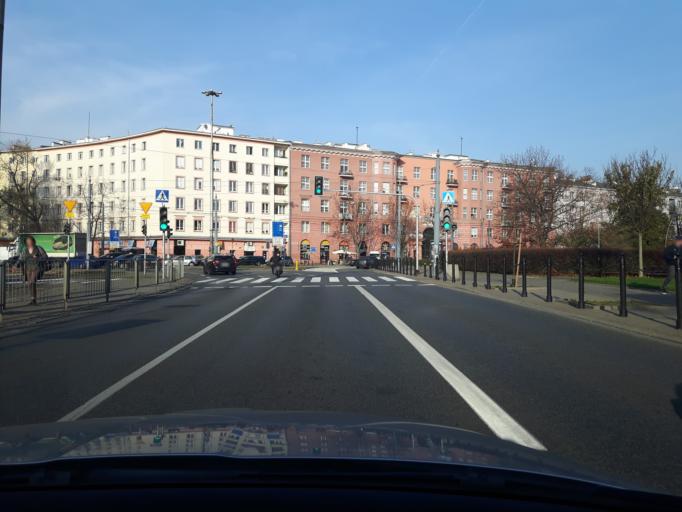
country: PL
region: Masovian Voivodeship
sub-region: Warszawa
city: Ochota
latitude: 52.2187
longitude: 20.9848
